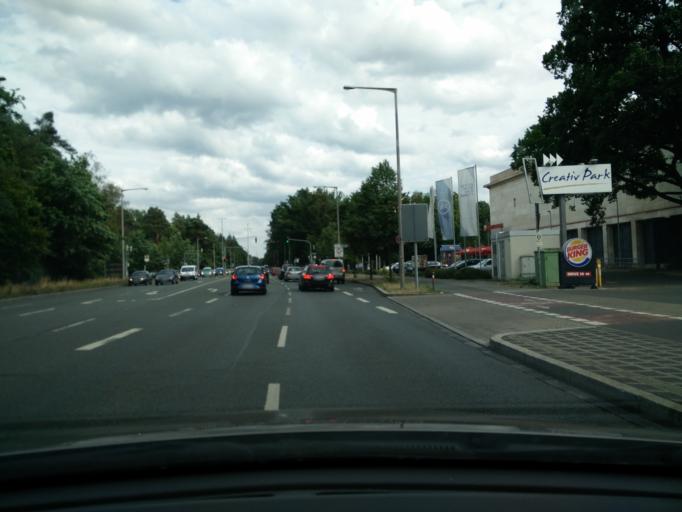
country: DE
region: Bavaria
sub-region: Regierungsbezirk Mittelfranken
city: Nuernberg
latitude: 49.4329
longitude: 11.1300
